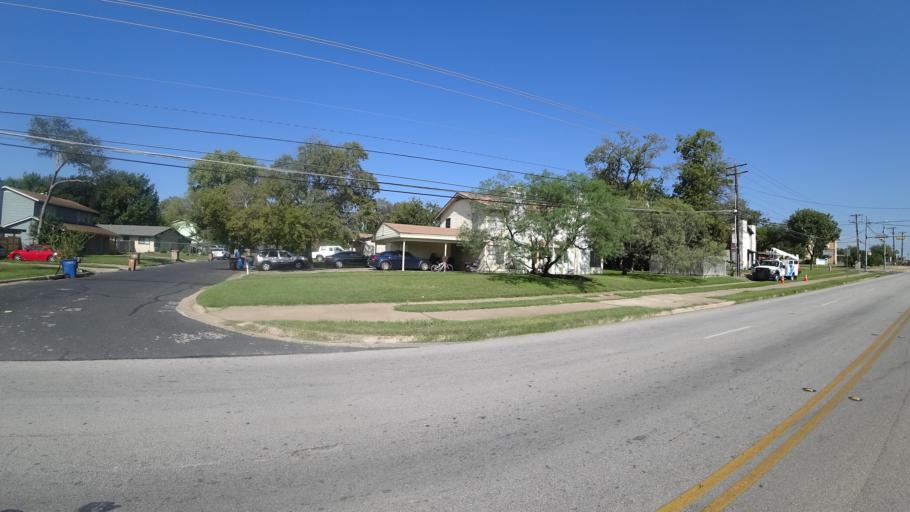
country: US
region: Texas
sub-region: Travis County
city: Austin
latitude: 30.3125
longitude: -97.6654
